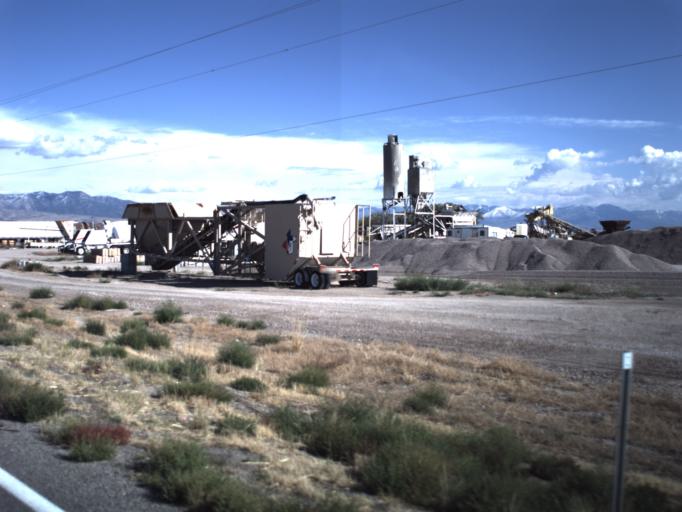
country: US
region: Utah
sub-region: Millard County
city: Delta
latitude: 39.3527
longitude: -112.5462
